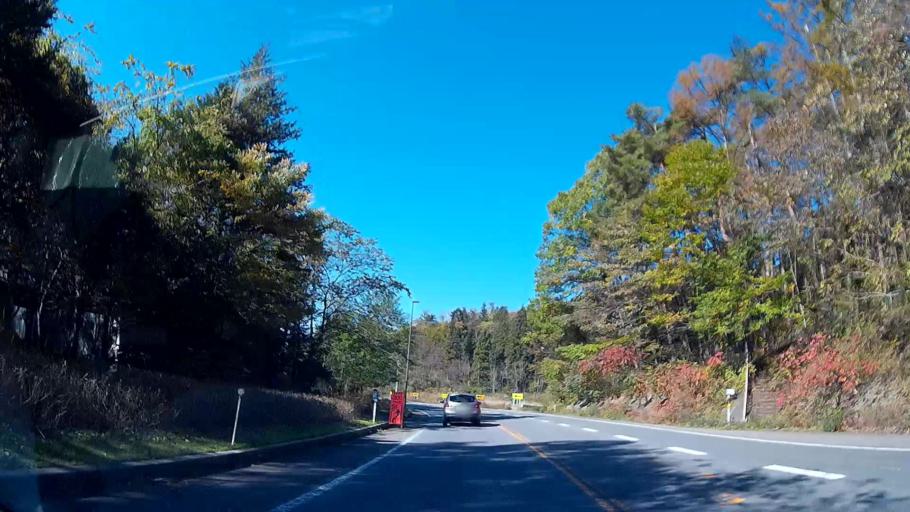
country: JP
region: Nagano
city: Okaya
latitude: 36.0902
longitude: 138.0244
